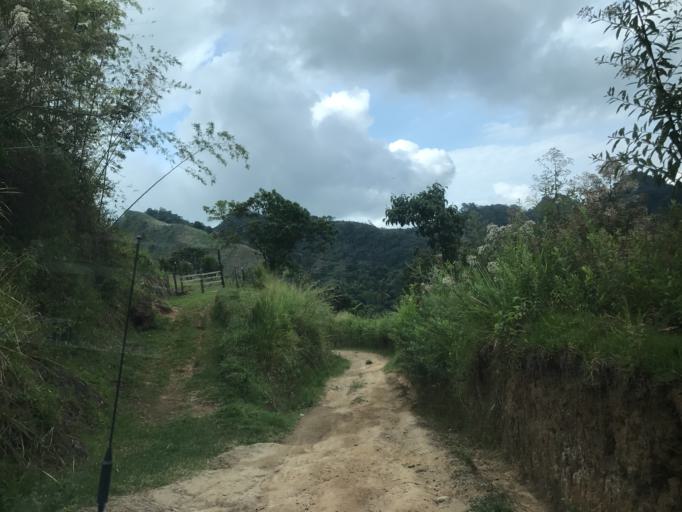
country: CO
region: Valle del Cauca
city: Obando
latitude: 4.5631
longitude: -75.8974
